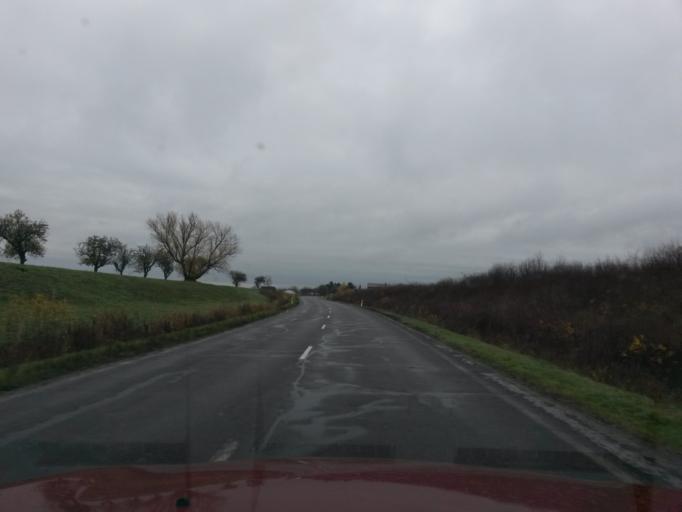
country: SK
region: Kosicky
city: Secovce
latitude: 48.6195
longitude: 21.5944
